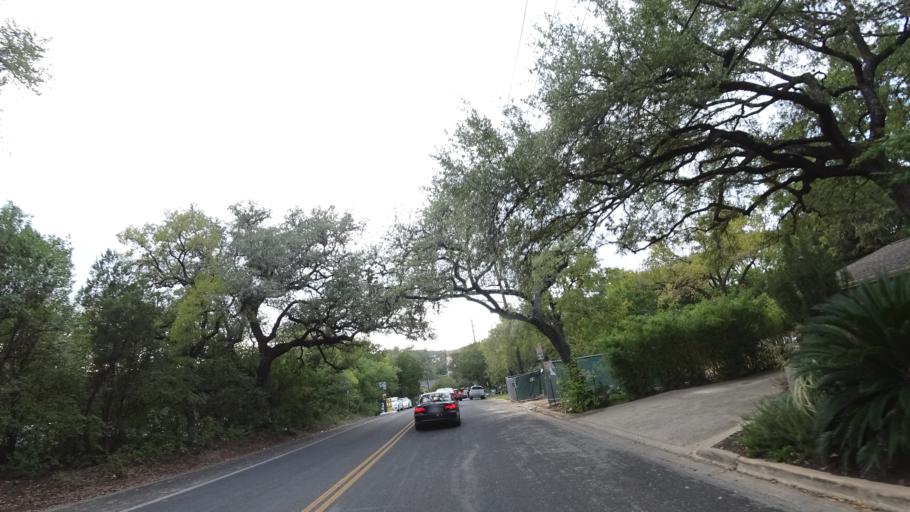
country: US
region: Texas
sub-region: Travis County
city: West Lake Hills
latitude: 30.2957
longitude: -97.7828
